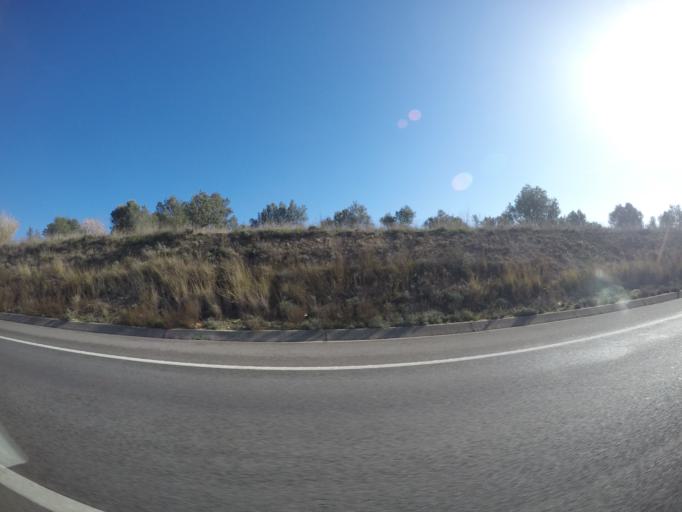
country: ES
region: Catalonia
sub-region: Provincia de Barcelona
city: Esparreguera
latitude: 41.5403
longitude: 1.8576
